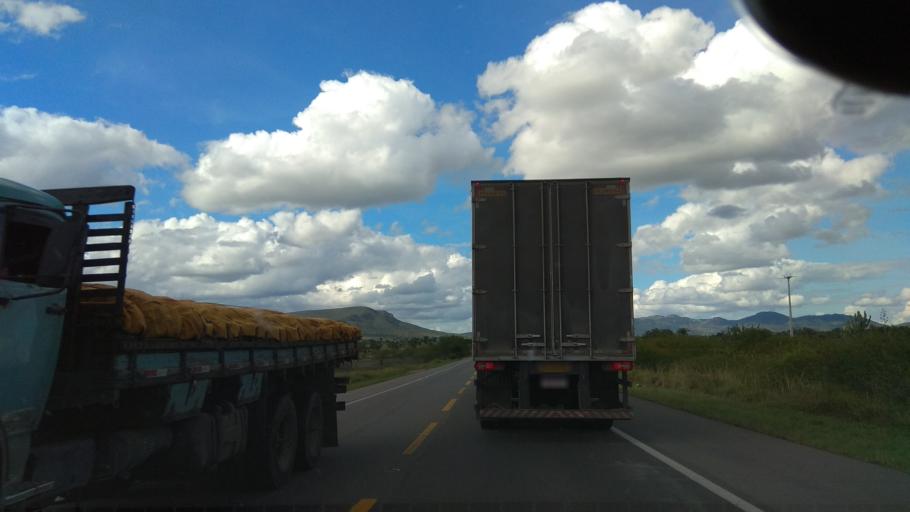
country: BR
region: Bahia
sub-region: Castro Alves
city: Castro Alves
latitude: -12.6768
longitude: -39.6632
